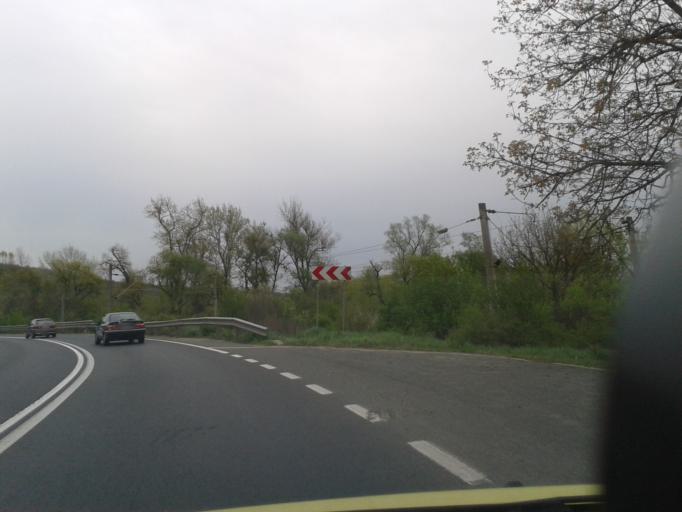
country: RO
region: Arad
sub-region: Comuna Bata
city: Bata
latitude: 46.0509
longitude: 22.0521
